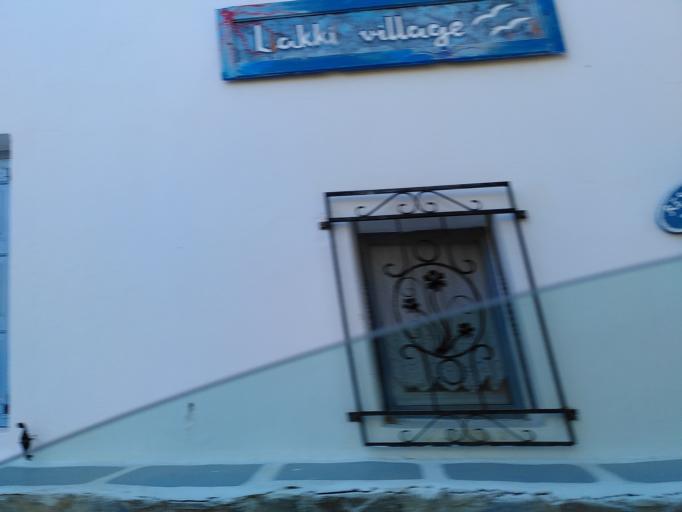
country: GR
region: South Aegean
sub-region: Nomos Kykladon
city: Amorgos
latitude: 36.9066
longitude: 25.9787
